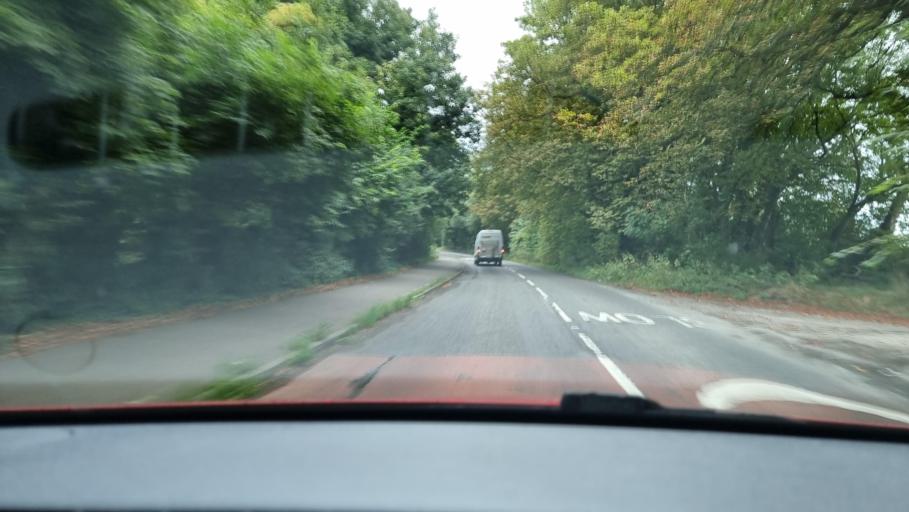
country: GB
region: England
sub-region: Hertfordshire
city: Tring
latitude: 51.7995
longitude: -0.6291
